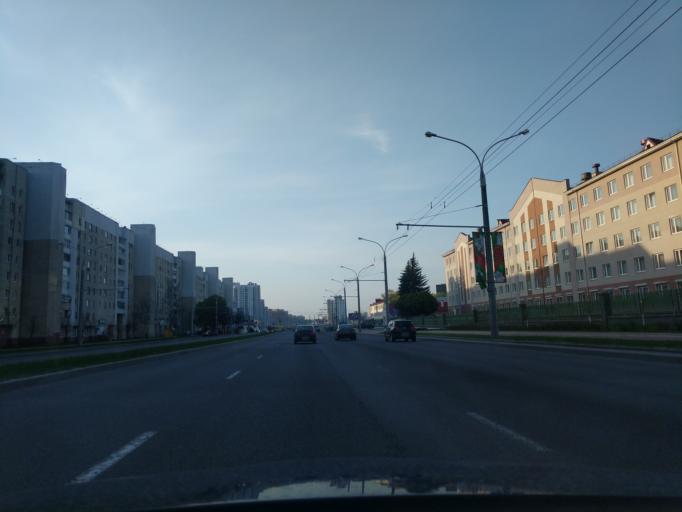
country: BY
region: Minsk
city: Minsk
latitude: 53.8670
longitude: 27.5707
